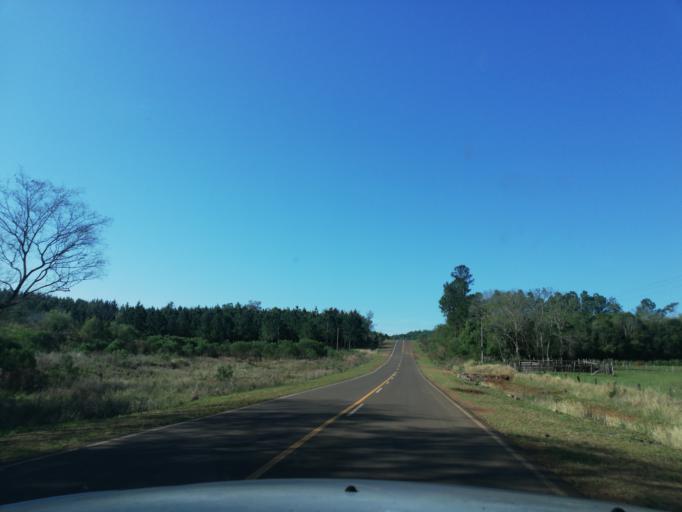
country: AR
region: Misiones
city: Arroyo del Medio
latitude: -27.6917
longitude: -55.4005
